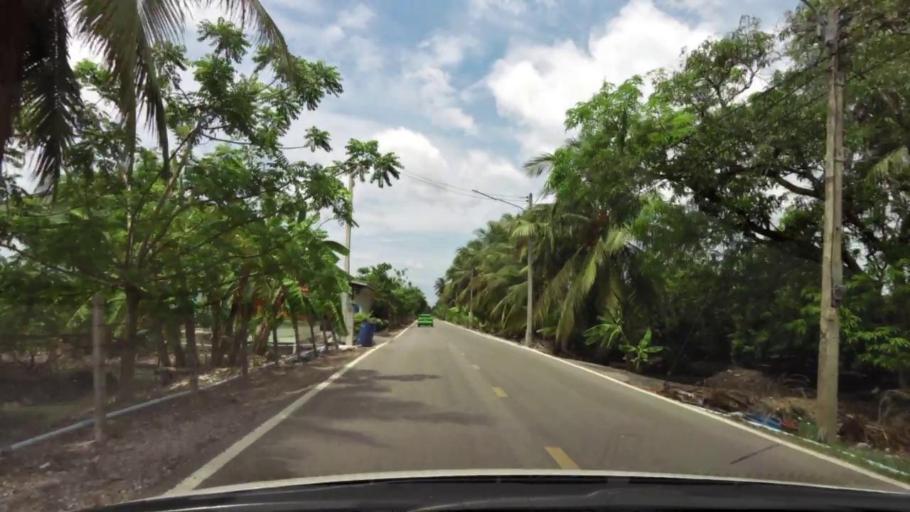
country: TH
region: Ratchaburi
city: Damnoen Saduak
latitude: 13.5257
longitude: 100.0124
